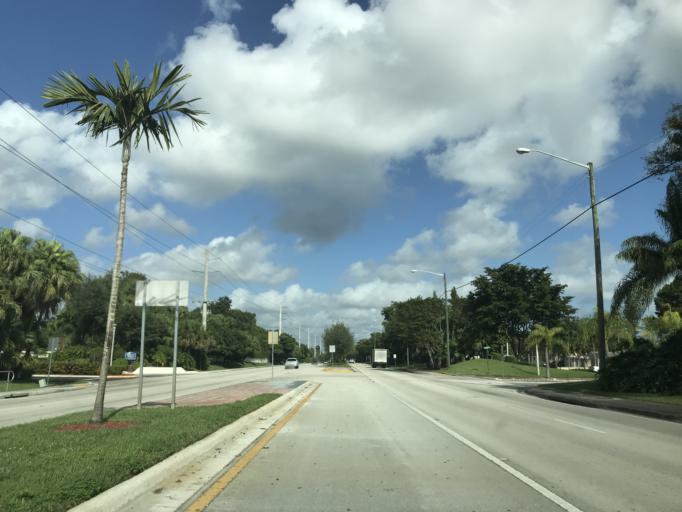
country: US
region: Florida
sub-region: Broward County
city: Coconut Creek
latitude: 26.2611
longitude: -80.1863
